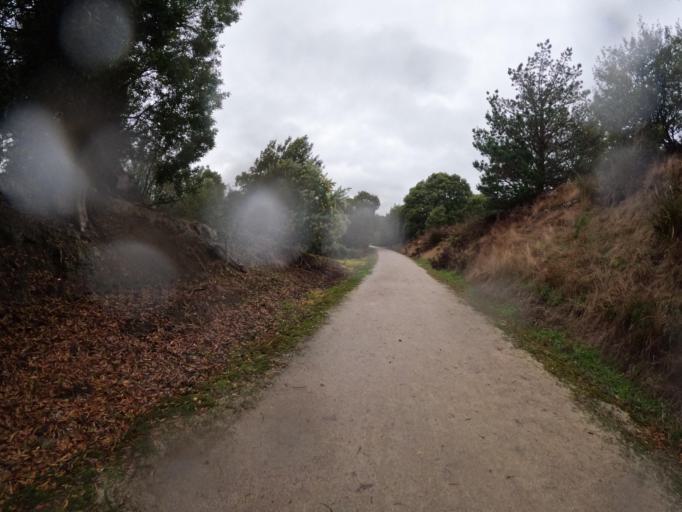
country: AU
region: Victoria
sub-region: Bass Coast
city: North Wonthaggi
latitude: -38.6954
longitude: 146.1031
